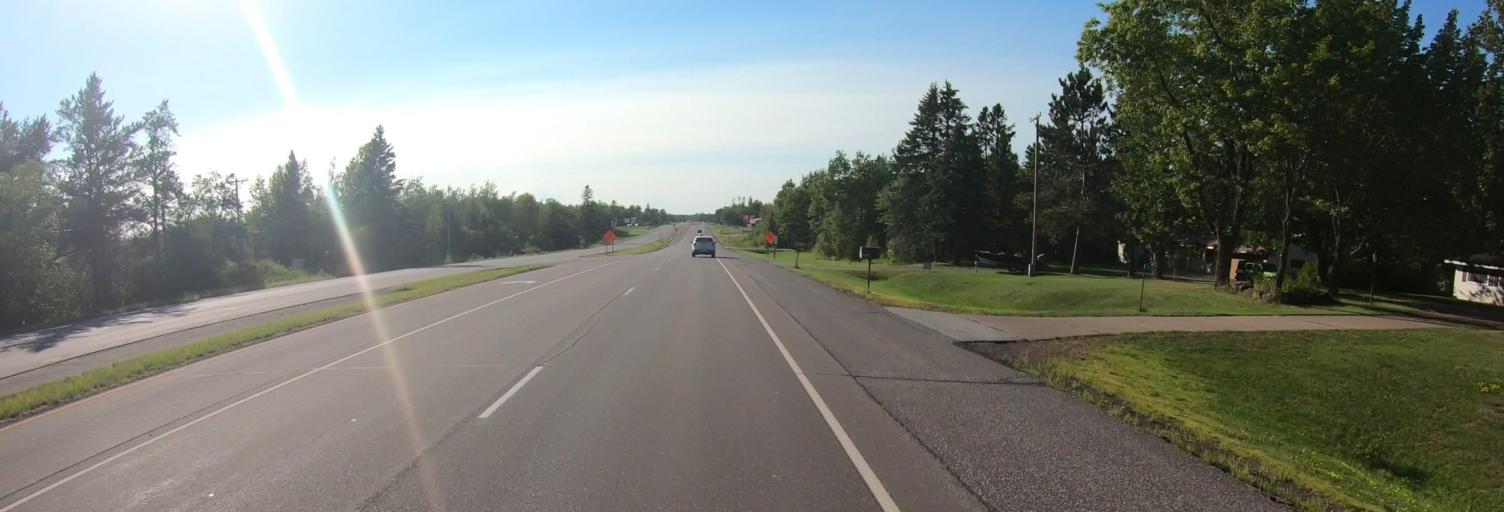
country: US
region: Minnesota
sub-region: Saint Louis County
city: Hermantown
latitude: 46.8467
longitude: -92.2663
